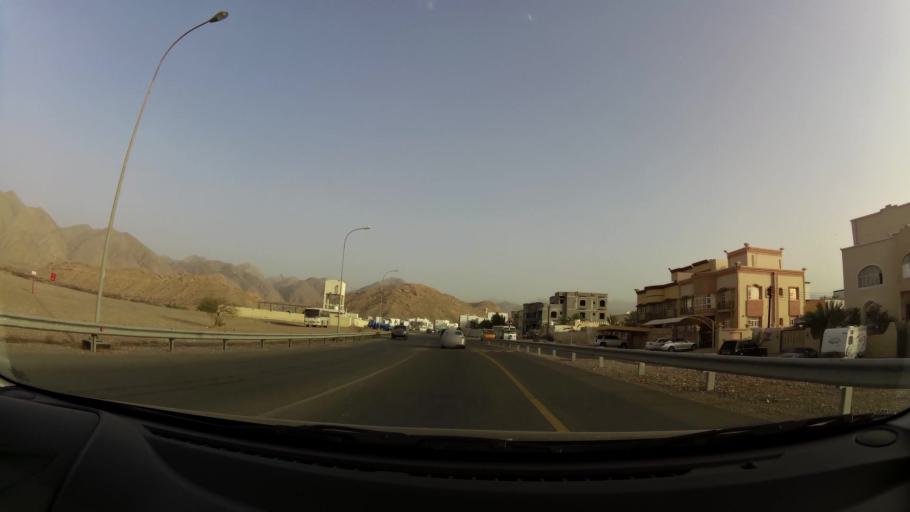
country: OM
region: Muhafazat Masqat
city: Bawshar
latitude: 23.5140
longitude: 58.3457
